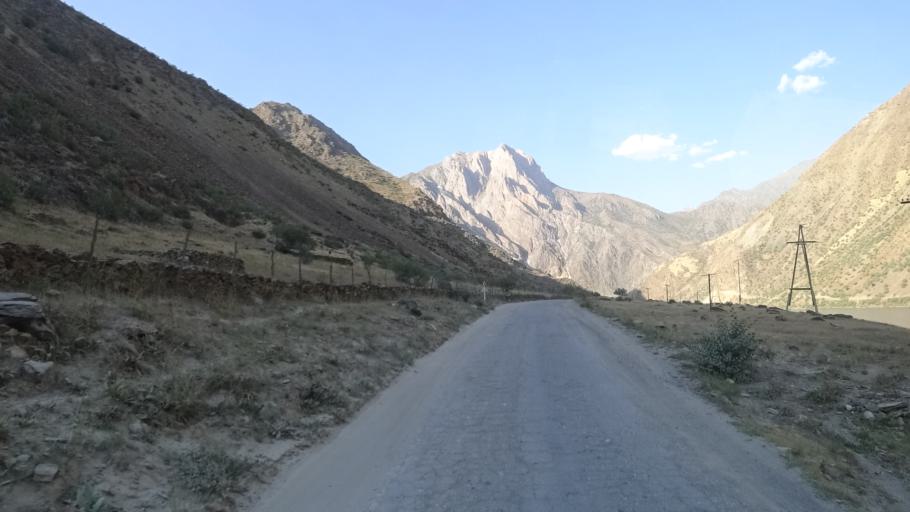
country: AF
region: Badakhshan
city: Maymay
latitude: 38.4770
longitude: 70.9682
